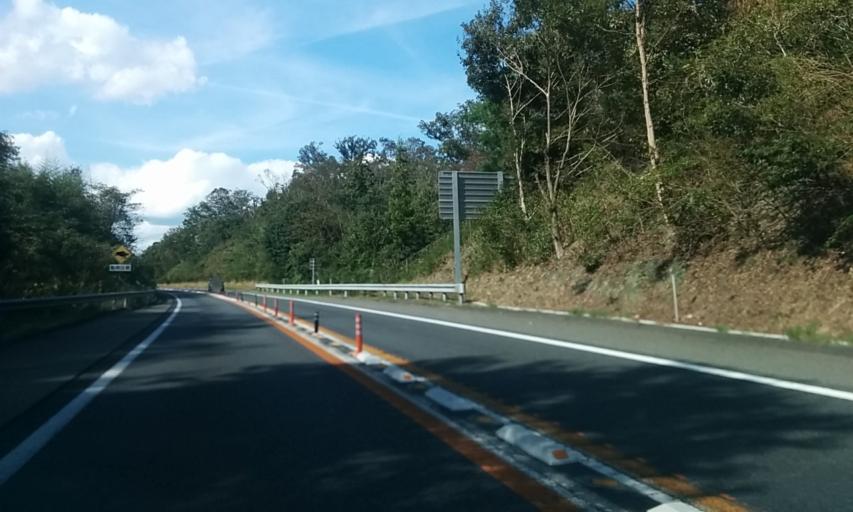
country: JP
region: Kyoto
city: Tanabe
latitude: 34.7823
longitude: 135.7727
